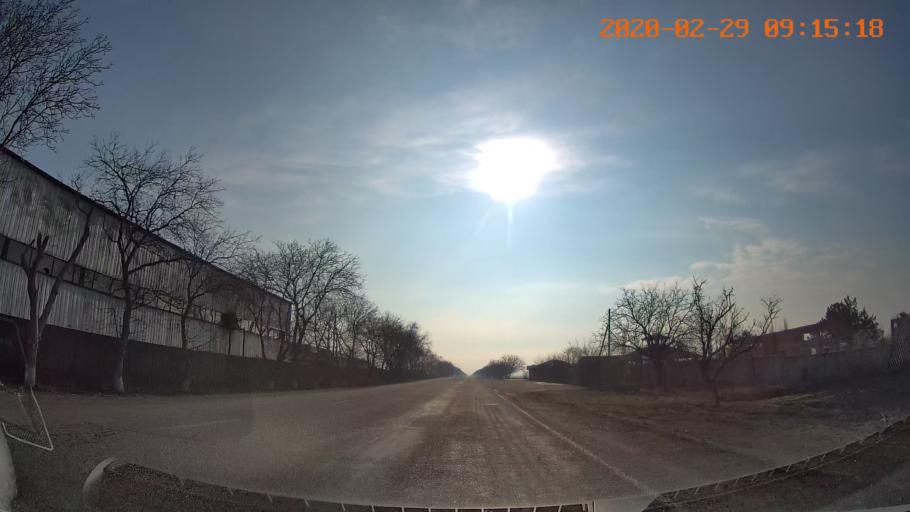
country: MD
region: Telenesti
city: Pervomaisc
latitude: 46.8018
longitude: 29.8666
